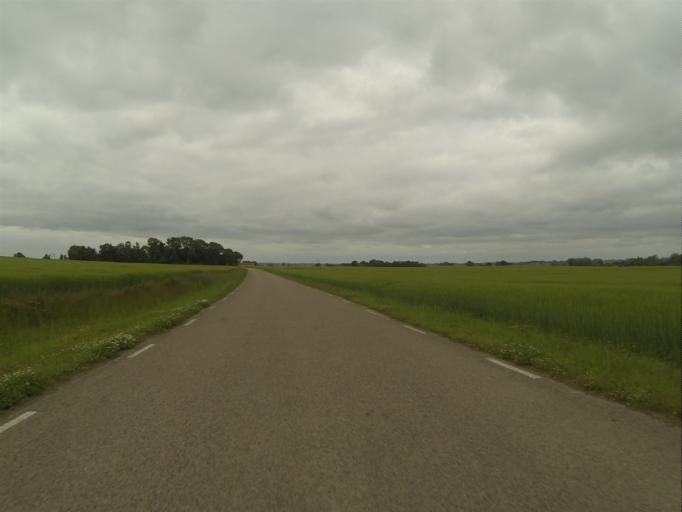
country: SE
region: Skane
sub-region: Staffanstorps Kommun
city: Staffanstorp
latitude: 55.6836
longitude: 13.2675
